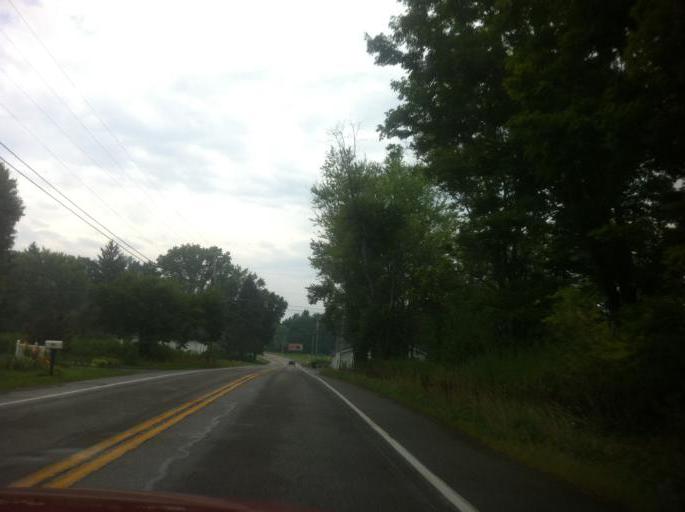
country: US
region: Pennsylvania
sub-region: Mercer County
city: Grove City
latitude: 41.1992
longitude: -80.0775
